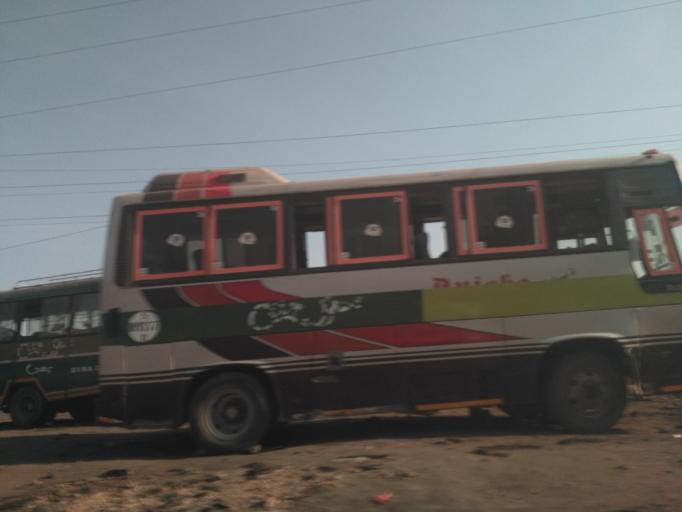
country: TZ
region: Dar es Salaam
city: Dar es Salaam
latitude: -6.9151
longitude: 39.2687
